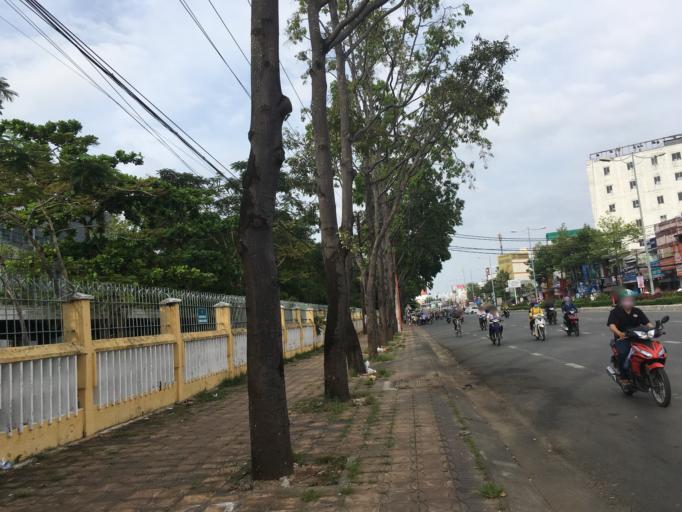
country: VN
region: Can Tho
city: Can Tho
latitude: 10.0293
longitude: 105.7714
